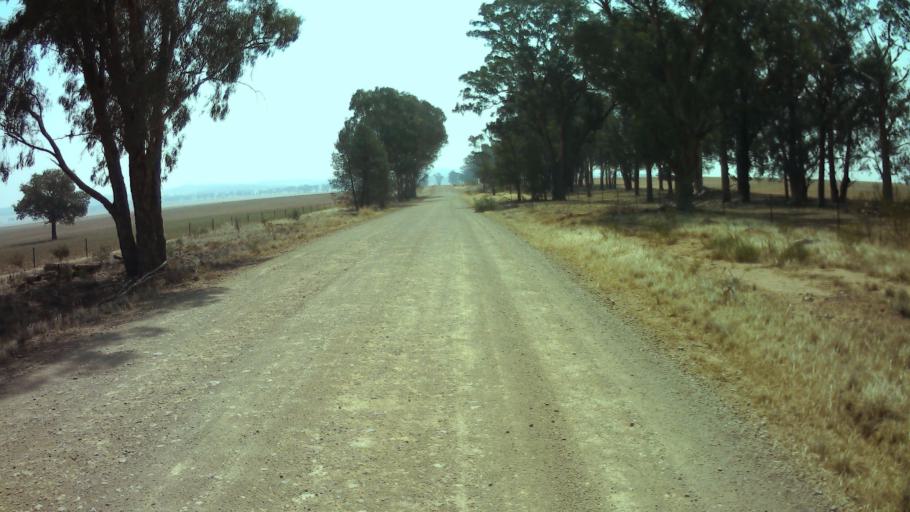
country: AU
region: New South Wales
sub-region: Weddin
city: Grenfell
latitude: -33.6372
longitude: 148.2245
